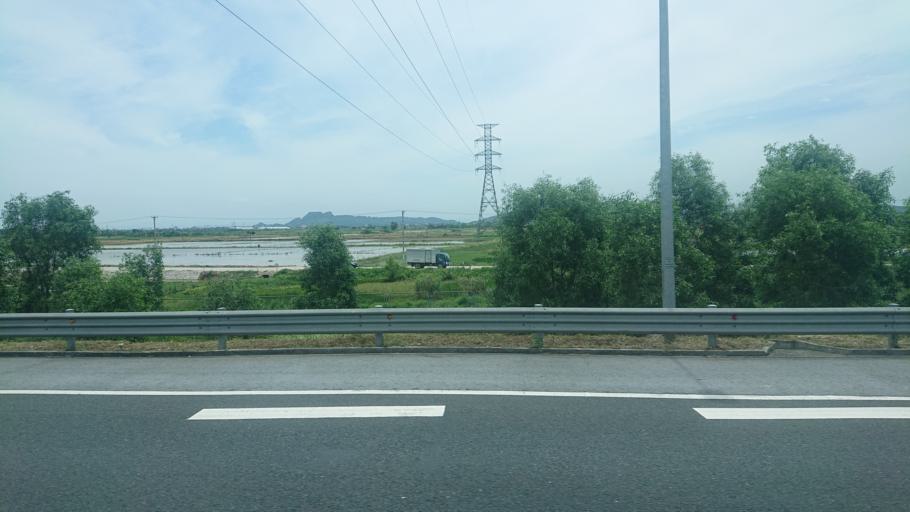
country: VN
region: Hai Phong
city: An Lao
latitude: 20.7913
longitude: 106.5518
